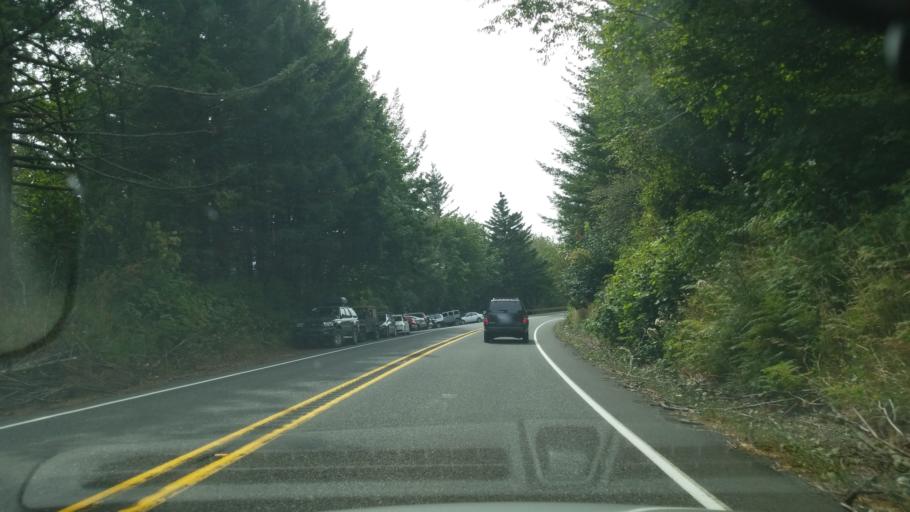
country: US
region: Washington
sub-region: Clark County
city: Washougal
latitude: 45.5665
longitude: -122.2123
